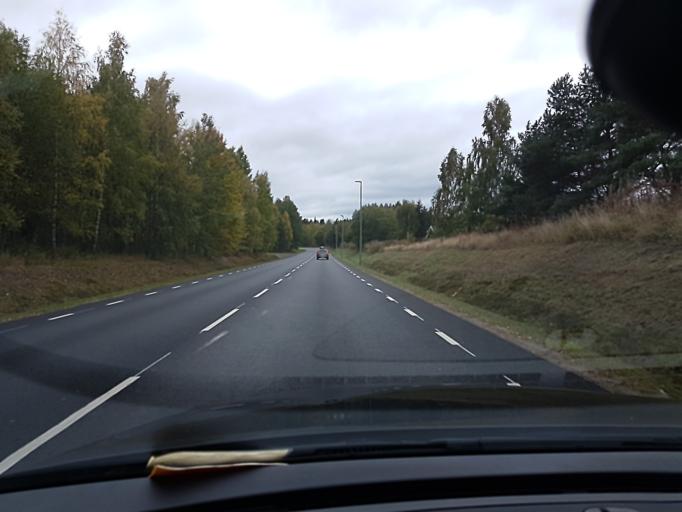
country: SE
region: Kronoberg
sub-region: Vaxjo Kommun
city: Vaexjoe
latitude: 56.9068
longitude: 14.7975
